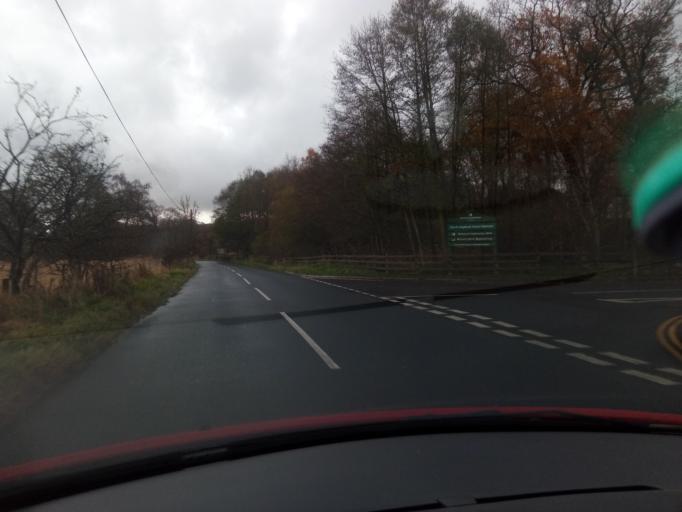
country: GB
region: England
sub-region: Northumberland
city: Birtley
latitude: 55.1366
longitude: -2.2582
